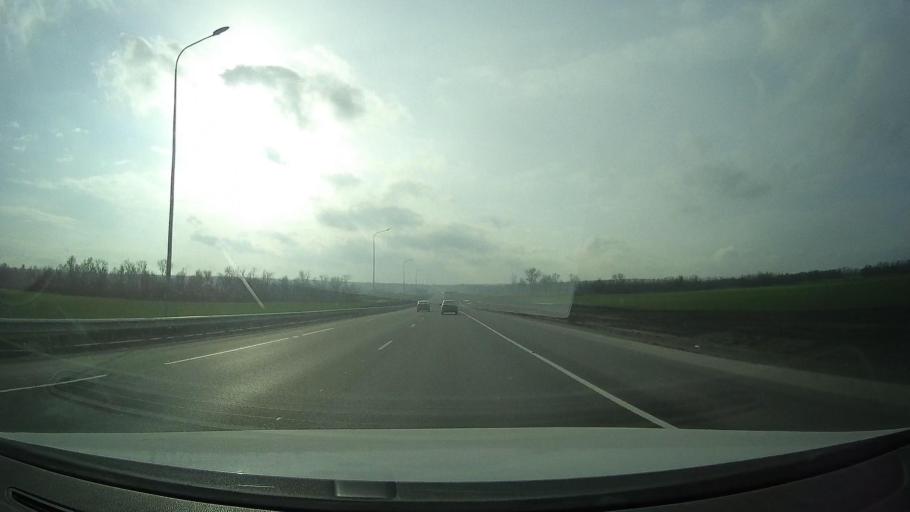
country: RU
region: Rostov
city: Grushevskaya
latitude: 47.4520
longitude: 39.8816
